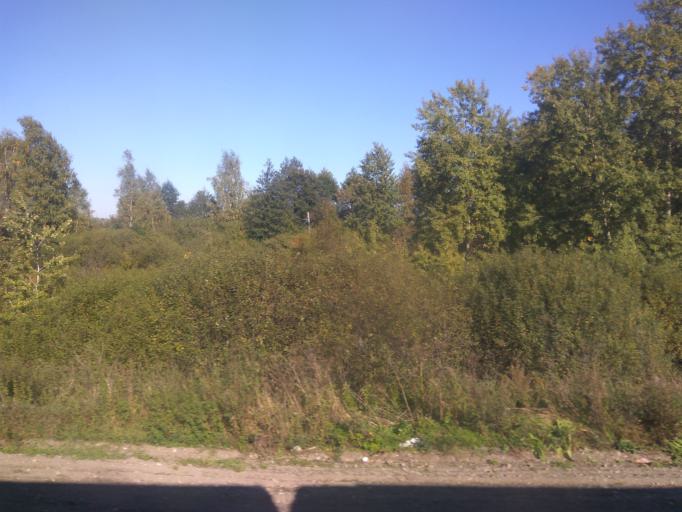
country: RU
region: Moskovskaya
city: Malyshevo
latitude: 55.5236
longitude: 38.3243
